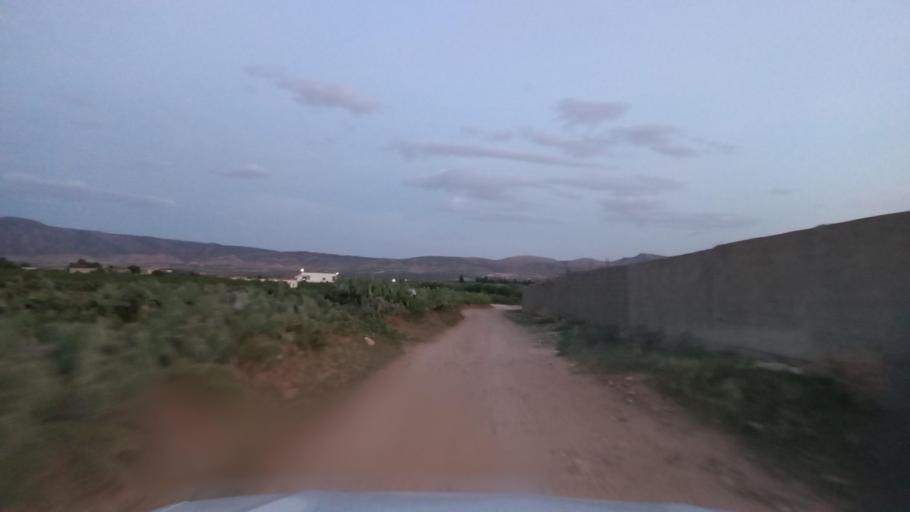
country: TN
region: Al Qasrayn
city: Sbiba
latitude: 35.4175
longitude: 9.1176
